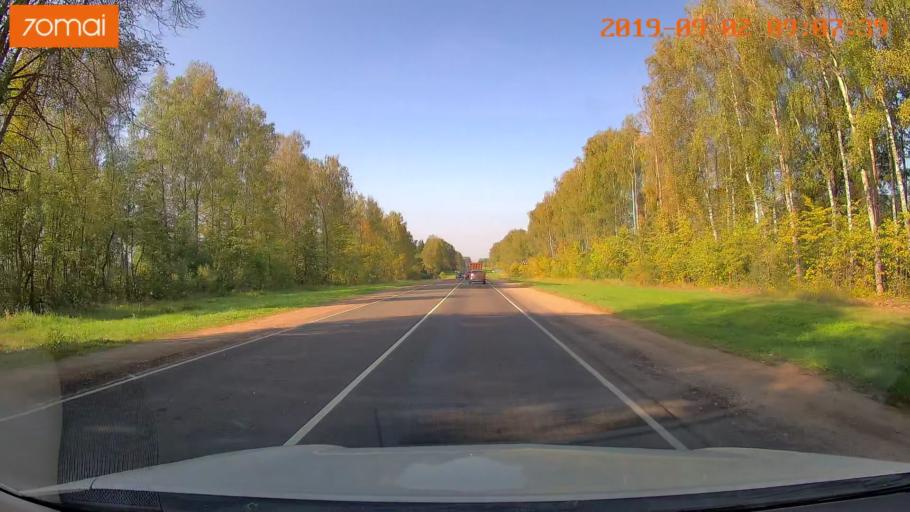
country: RU
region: Kaluga
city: Myatlevo
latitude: 54.8945
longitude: 35.6542
